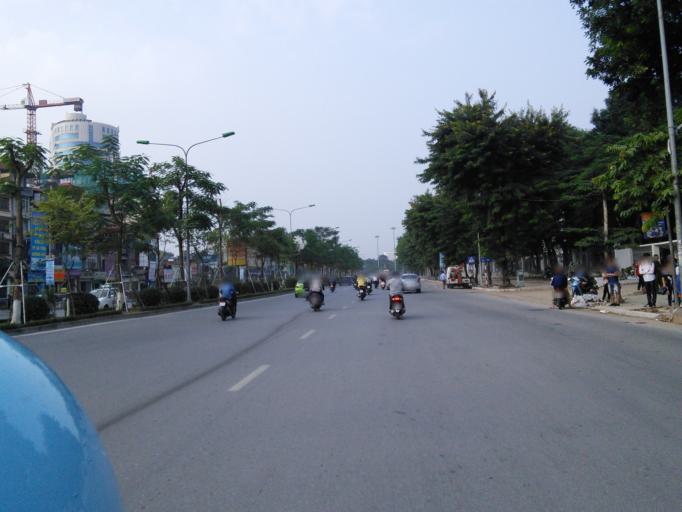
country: VN
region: Ha Noi
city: Hai BaTrung
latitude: 21.0049
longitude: 105.8415
